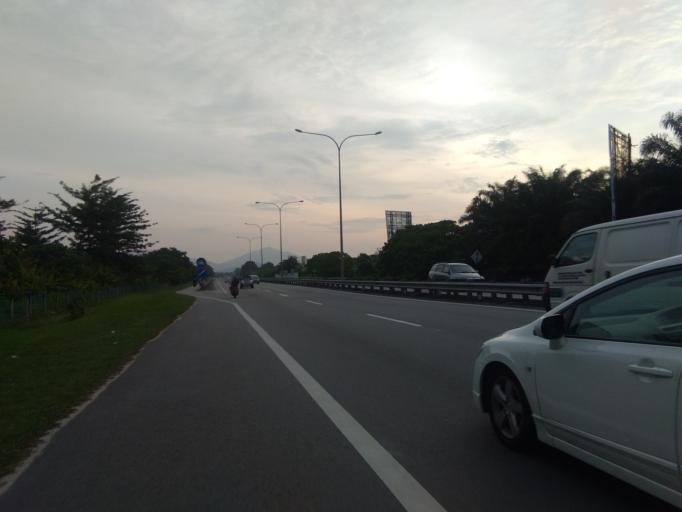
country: MY
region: Kedah
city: Kulim
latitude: 5.4308
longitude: 100.5491
